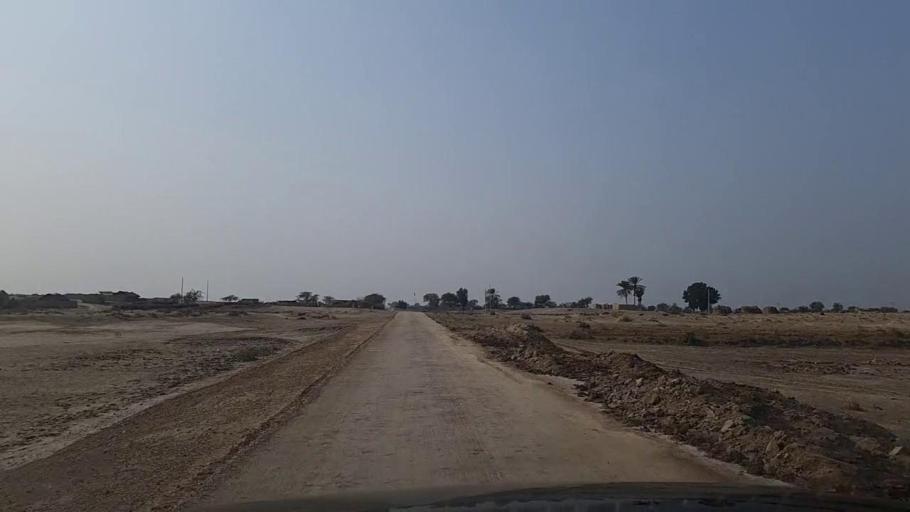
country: PK
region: Sindh
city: Daur
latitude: 26.3858
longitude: 68.4115
